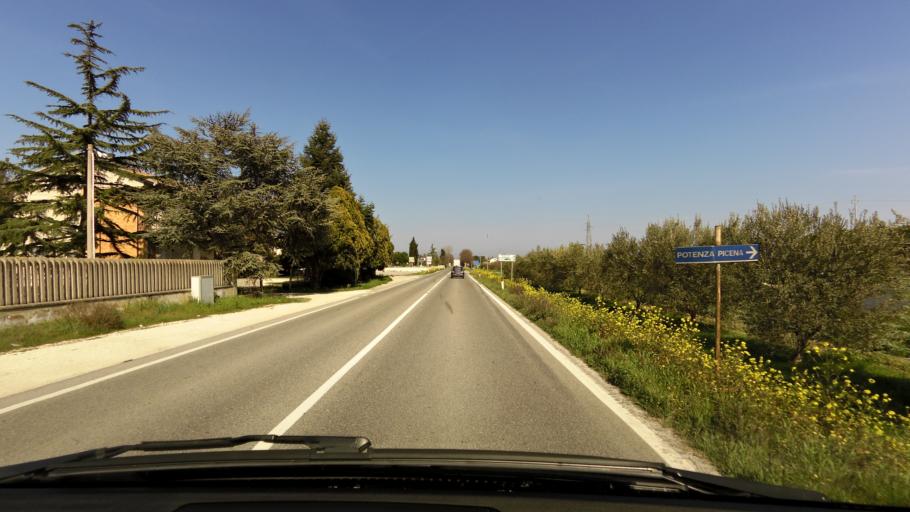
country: IT
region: The Marches
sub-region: Provincia di Macerata
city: Potenza Picena
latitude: 43.3948
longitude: 13.6440
